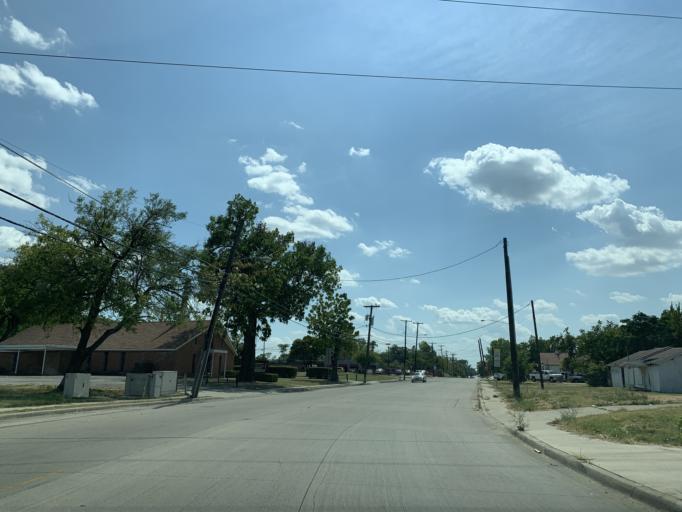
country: US
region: Texas
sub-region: Dallas County
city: Dallas
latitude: 32.7105
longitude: -96.7744
